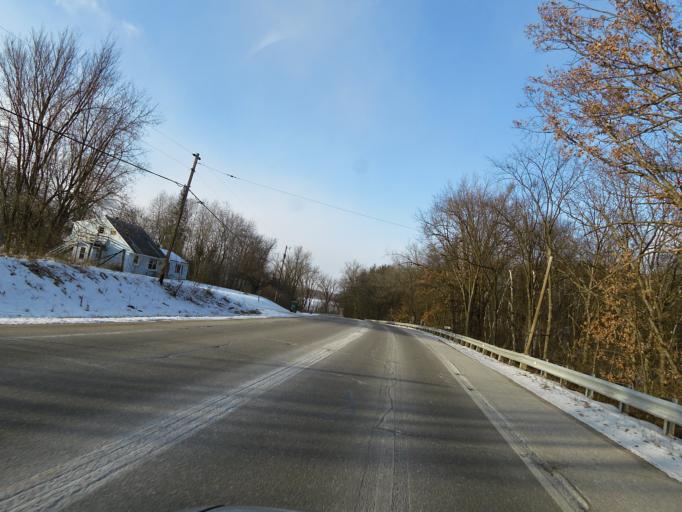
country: US
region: Minnesota
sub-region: Washington County
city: Lake Elmo
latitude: 44.9739
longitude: -92.8830
